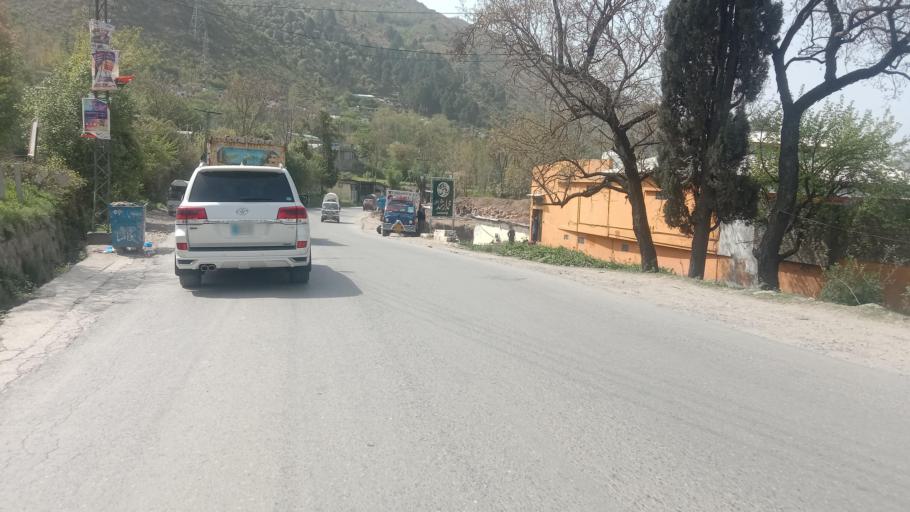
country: PK
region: Khyber Pakhtunkhwa
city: Abbottabad
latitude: 34.1293
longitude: 73.1982
